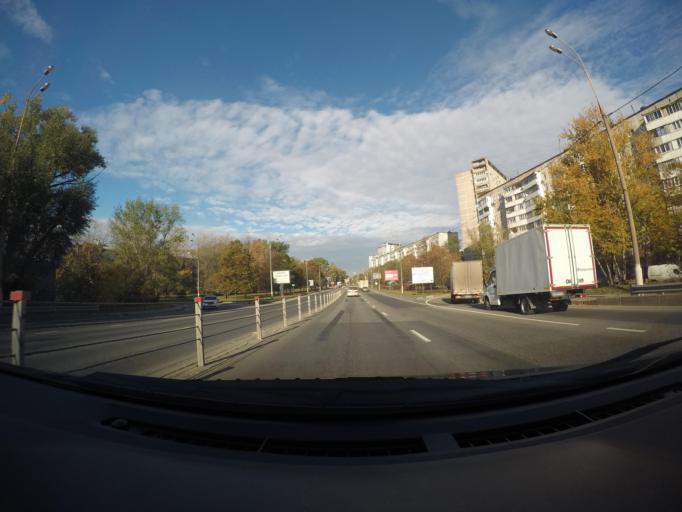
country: RU
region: Moskovskaya
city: Mytishchi
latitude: 55.9208
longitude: 37.7625
